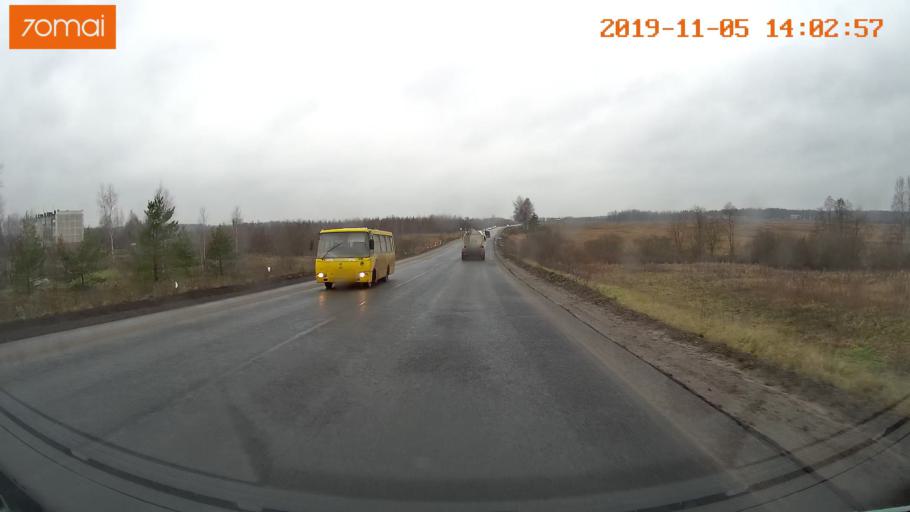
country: RU
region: Ivanovo
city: Kokhma
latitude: 56.9991
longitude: 41.2044
